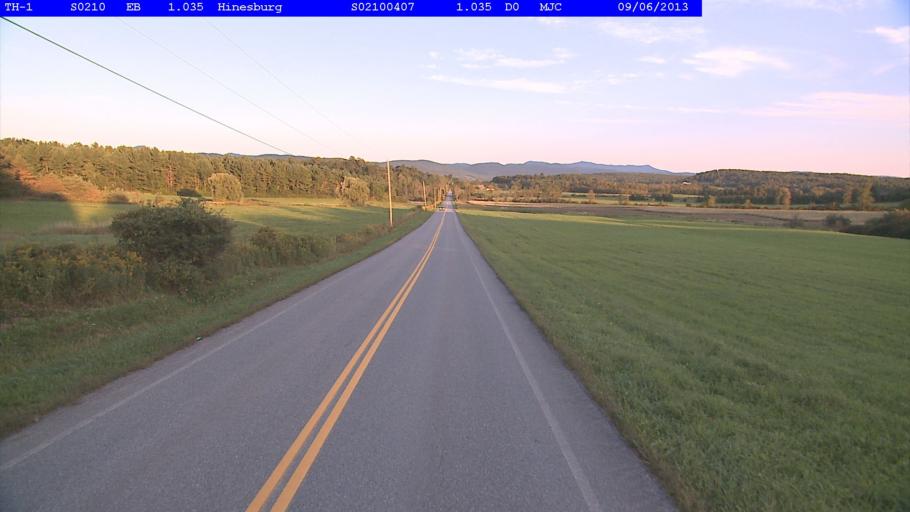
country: US
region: Vermont
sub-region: Chittenden County
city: Hinesburg
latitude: 44.3502
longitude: -73.1504
